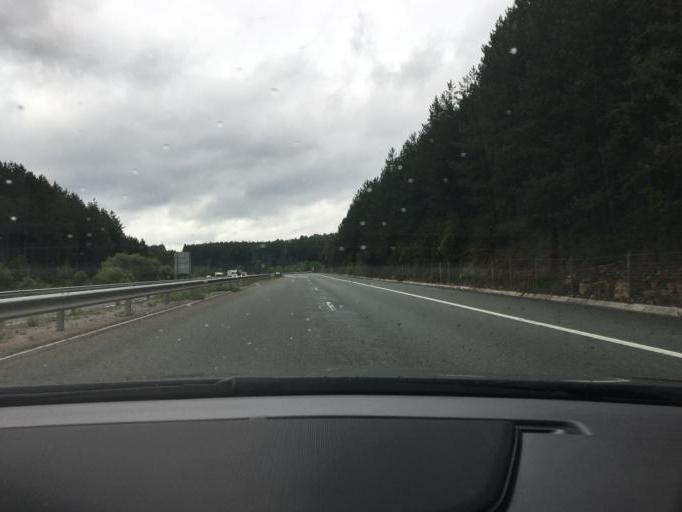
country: BG
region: Pernik
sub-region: Obshtina Pernik
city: Pernik
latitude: 42.5255
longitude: 23.1342
